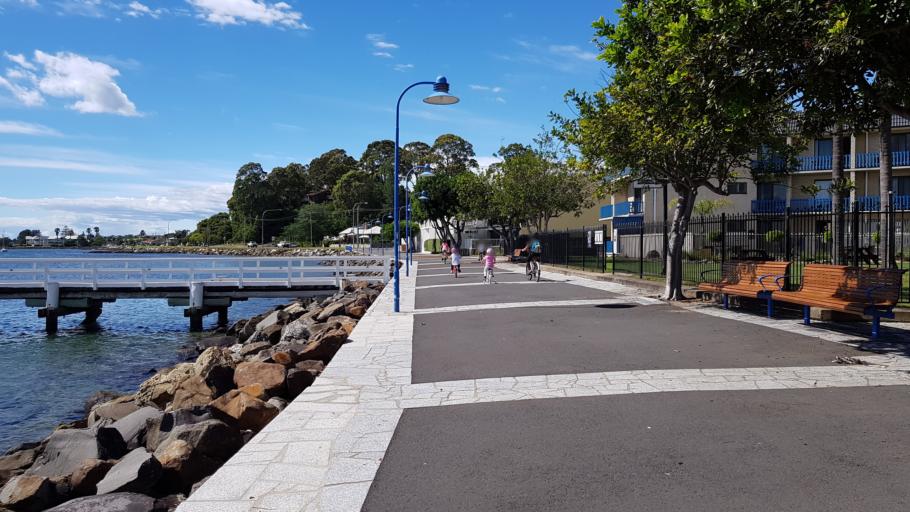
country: AU
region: New South Wales
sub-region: Eurobodalla
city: Batemans Bay
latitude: -35.7076
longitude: 150.1790
